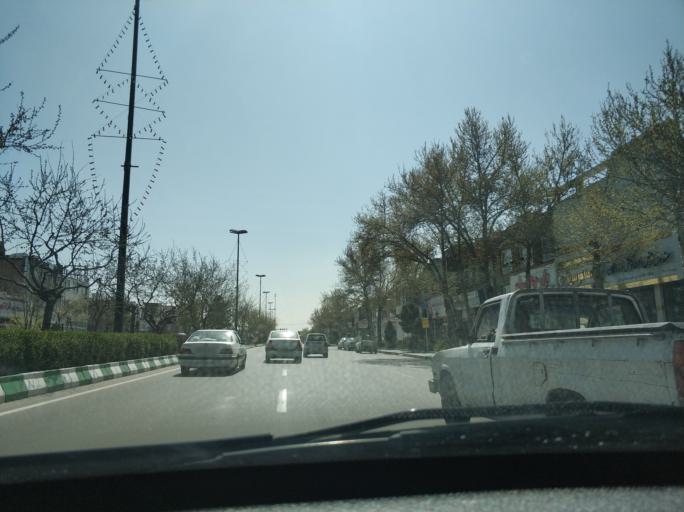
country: IR
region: Razavi Khorasan
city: Mashhad
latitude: 36.2597
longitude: 59.6071
